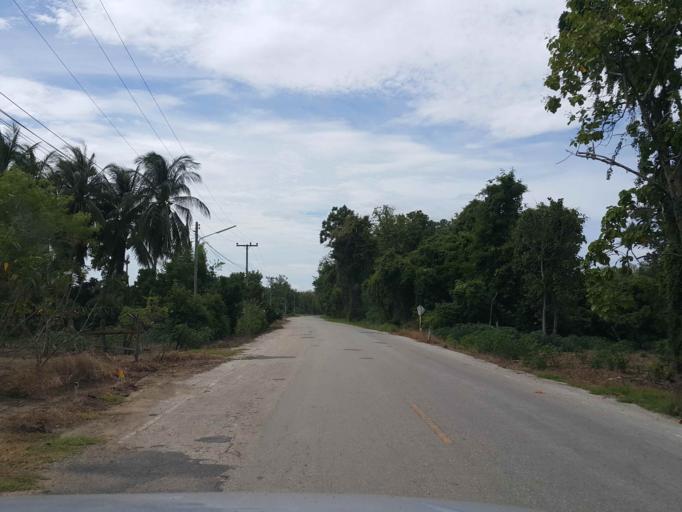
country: TH
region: Sukhothai
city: Ban Dan Lan Hoi
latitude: 17.0857
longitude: 99.4776
